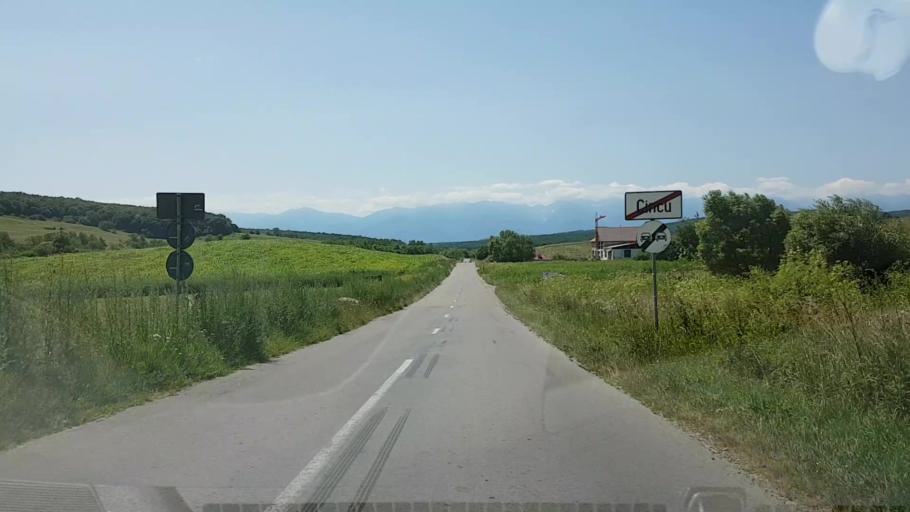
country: RO
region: Brasov
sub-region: Comuna Cincu
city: Cincu
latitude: 45.9058
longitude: 24.8116
